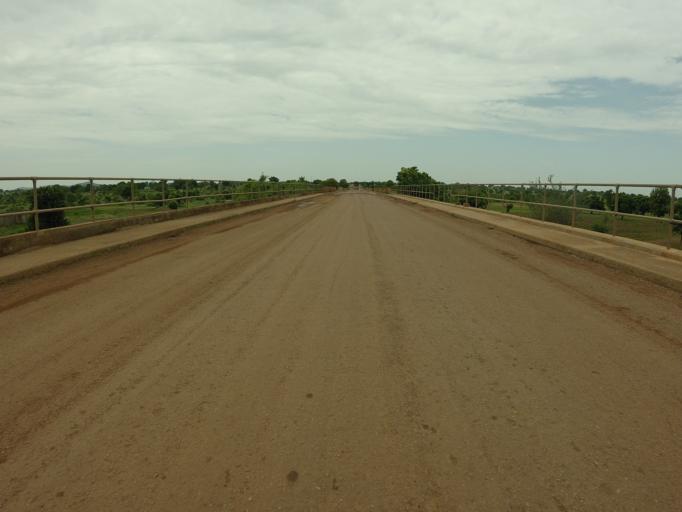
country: GH
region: Upper East
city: Bawku
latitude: 11.0026
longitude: -0.3840
